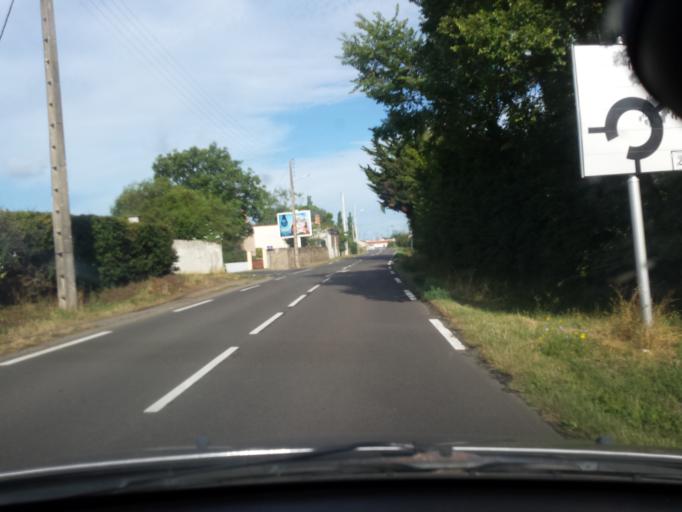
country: FR
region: Pays de la Loire
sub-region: Departement de la Vendee
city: Olonne-sur-Mer
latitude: 46.5394
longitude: -1.7925
